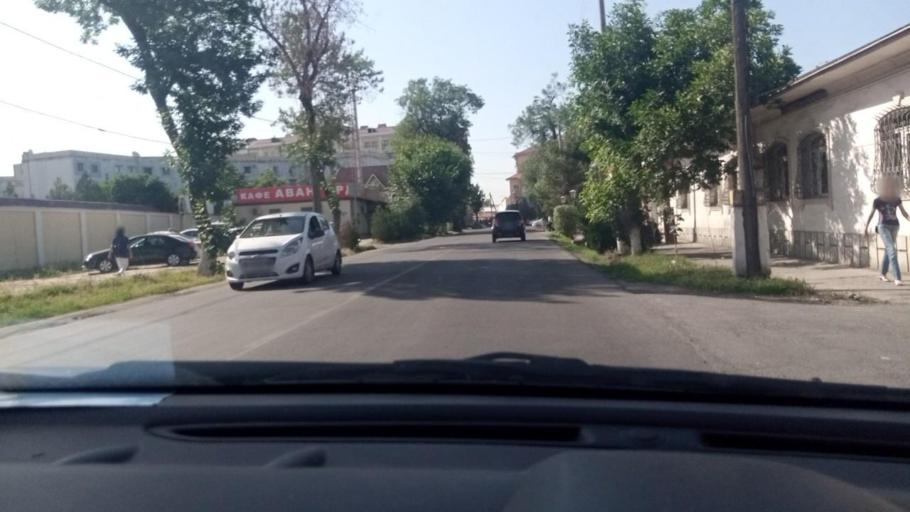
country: UZ
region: Toshkent Shahri
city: Tashkent
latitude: 41.2821
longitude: 69.2850
